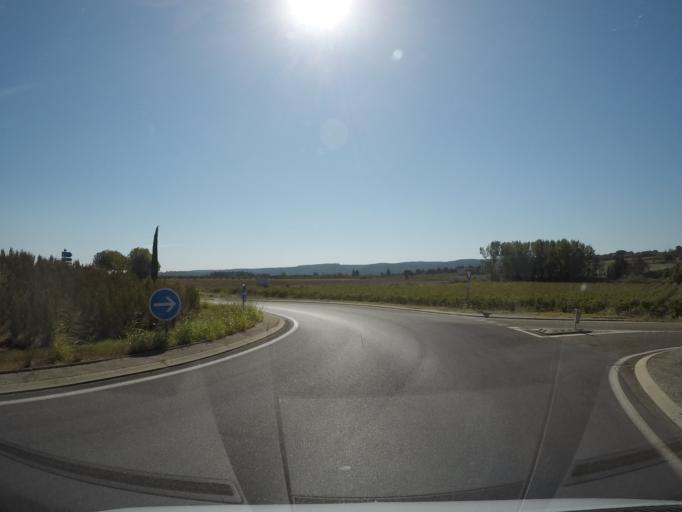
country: FR
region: Languedoc-Roussillon
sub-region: Departement du Gard
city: Castillon-du-Gard
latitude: 43.9719
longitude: 4.4976
